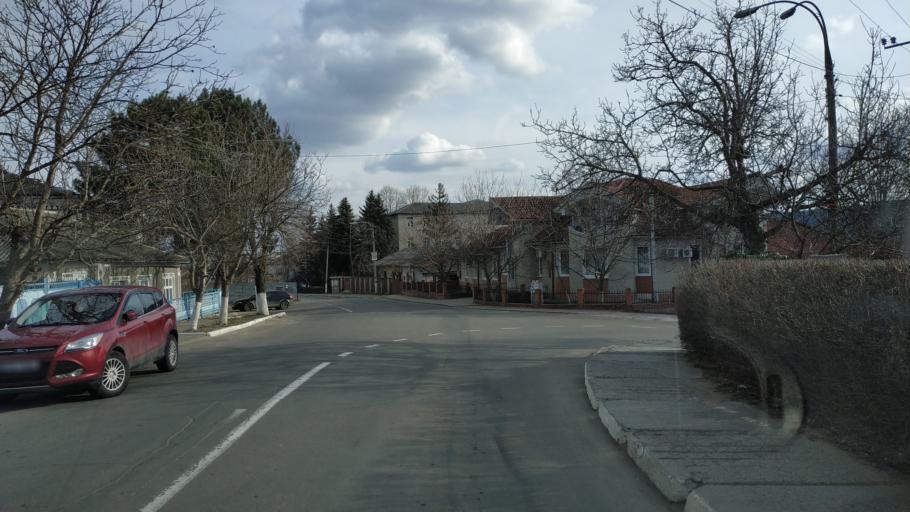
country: MD
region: Hincesti
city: Hincesti
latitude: 46.8315
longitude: 28.5850
